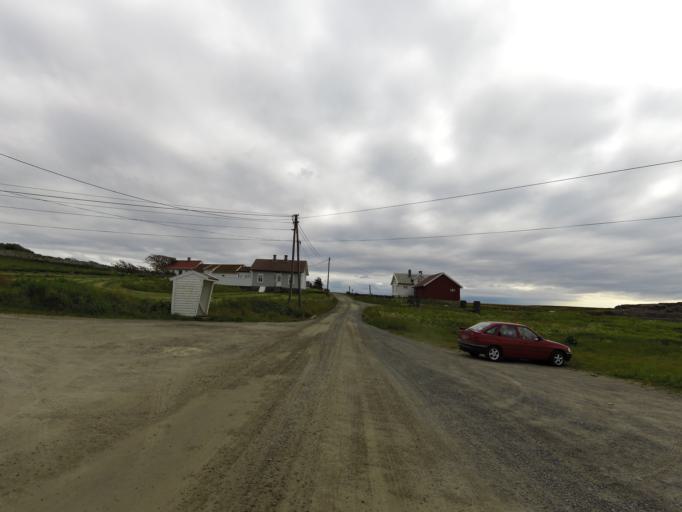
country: NO
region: Vest-Agder
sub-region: Farsund
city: Vestbygd
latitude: 58.1390
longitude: 6.6062
